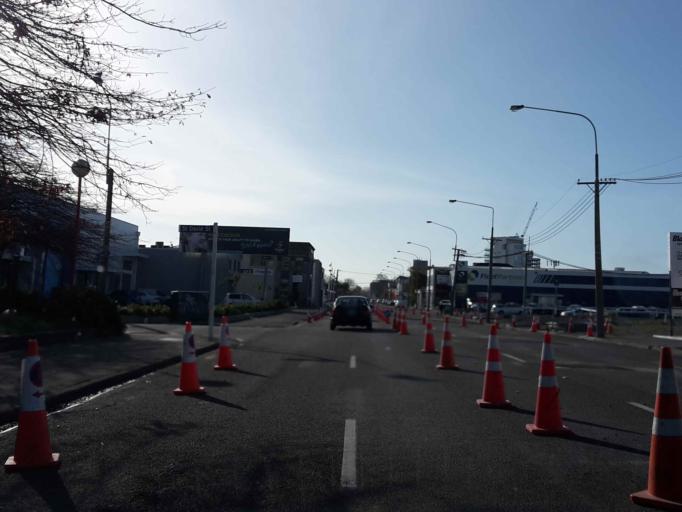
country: NZ
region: Canterbury
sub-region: Christchurch City
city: Christchurch
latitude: -43.5394
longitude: 172.6306
